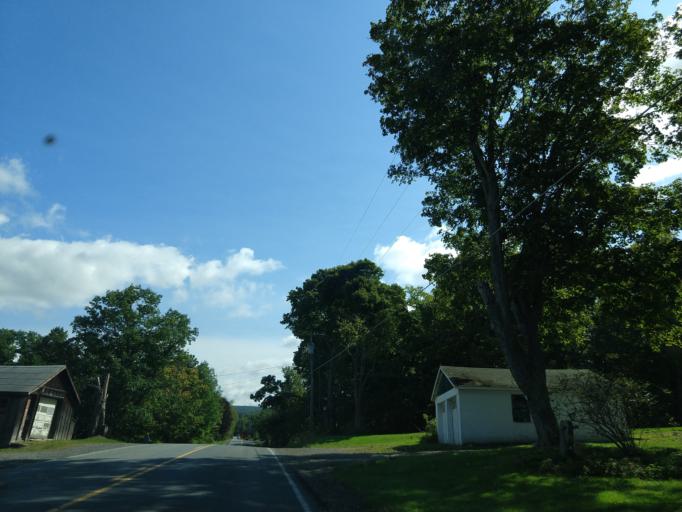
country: US
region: New York
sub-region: Tompkins County
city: East Ithaca
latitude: 42.4081
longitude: -76.4696
